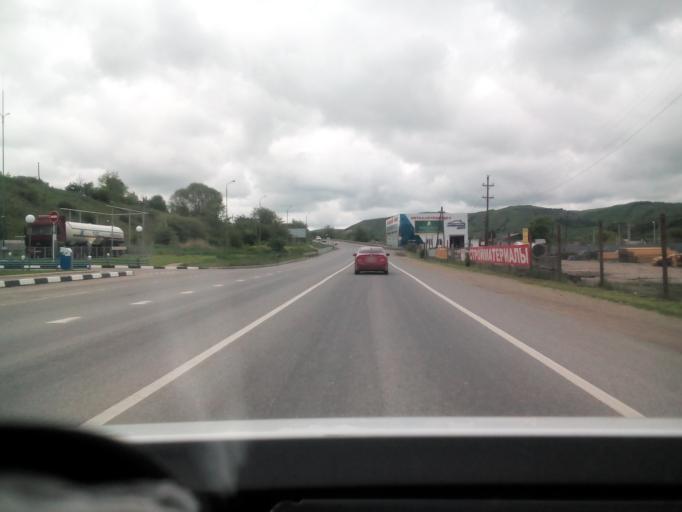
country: RU
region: Stavropol'skiy
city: Yasnaya Polyana
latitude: 43.9640
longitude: 42.7746
